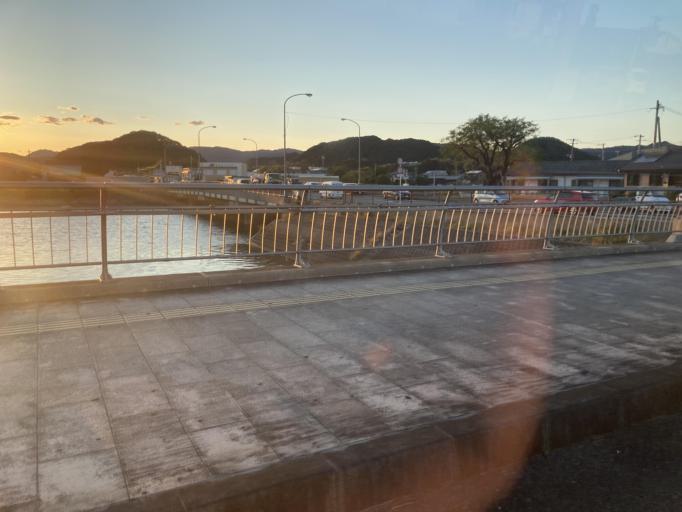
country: JP
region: Miyazaki
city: Nobeoka
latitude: 32.4177
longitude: 131.6254
